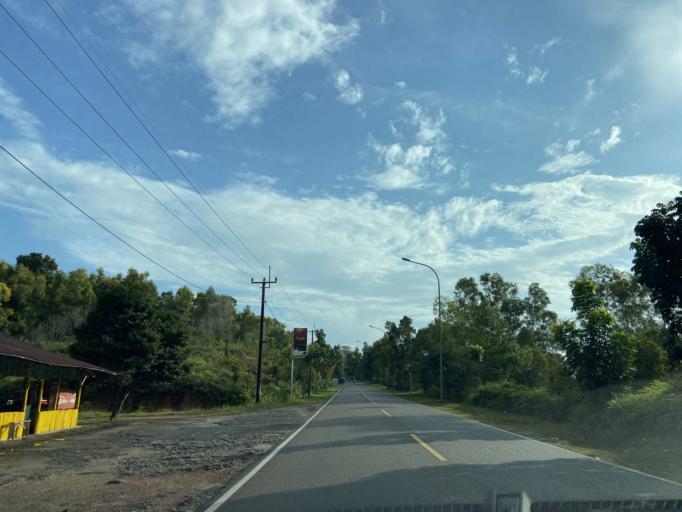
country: SG
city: Singapore
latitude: 0.9631
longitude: 104.0556
